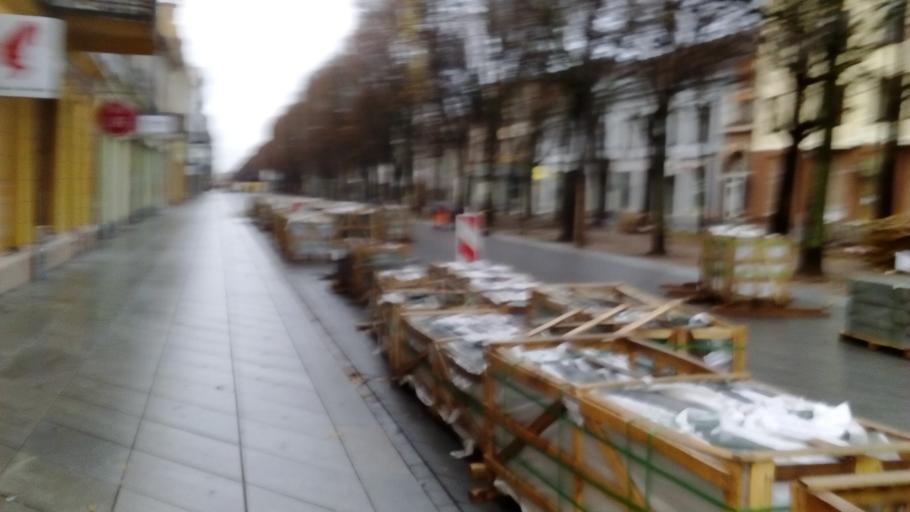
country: LT
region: Kauno apskritis
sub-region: Kaunas
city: Kaunas
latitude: 54.8973
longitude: 23.9175
